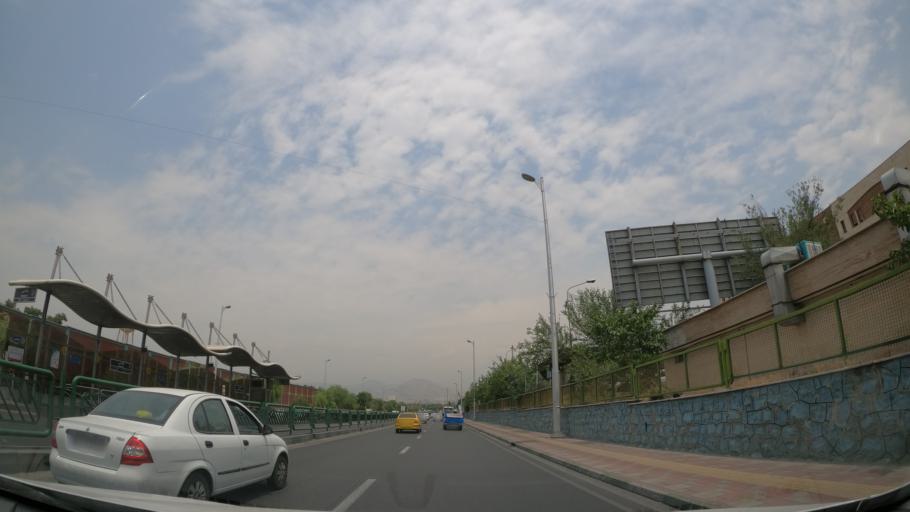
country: IR
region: Tehran
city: Tehran
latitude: 35.6893
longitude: 51.3406
